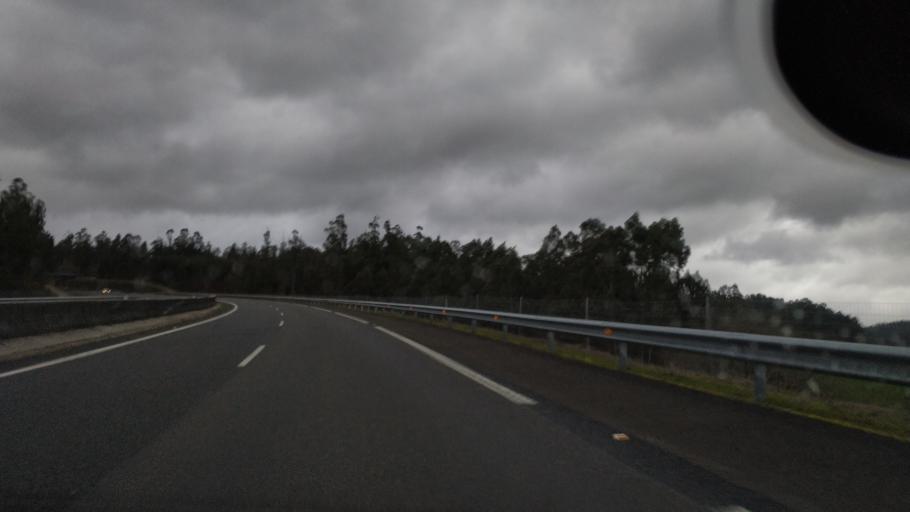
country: ES
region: Galicia
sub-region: Provincia da Coruna
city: Vedra
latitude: 42.8189
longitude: -8.4890
